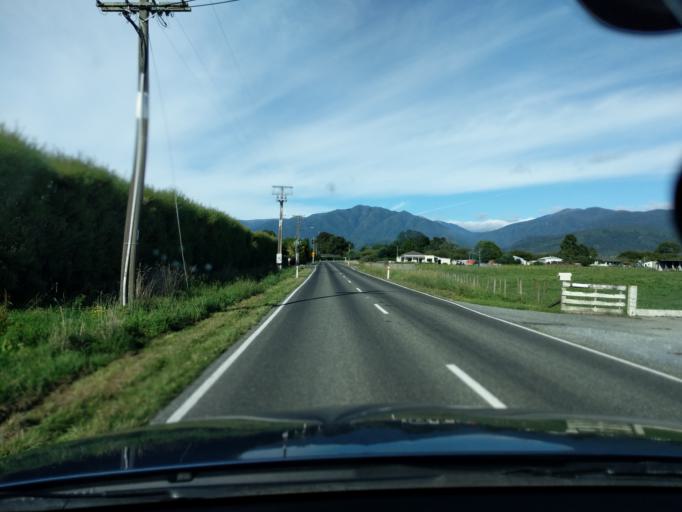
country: NZ
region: Tasman
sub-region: Tasman District
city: Takaka
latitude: -40.8563
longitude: 172.8235
